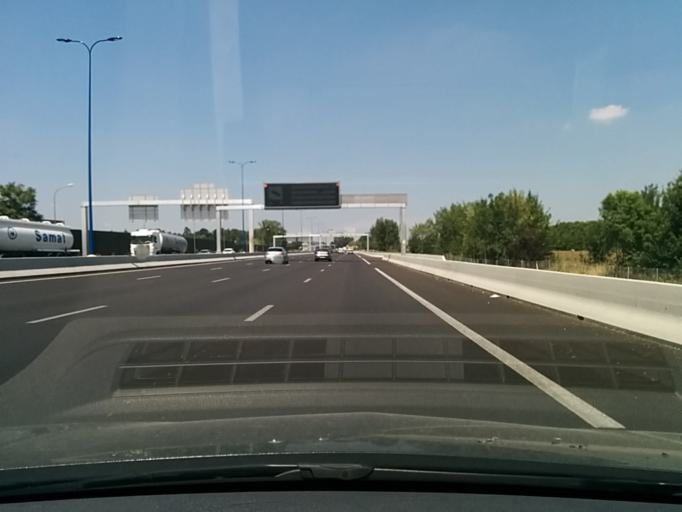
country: FR
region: Midi-Pyrenees
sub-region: Departement de la Haute-Garonne
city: Ramonville-Saint-Agne
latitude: 43.5639
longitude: 1.4865
